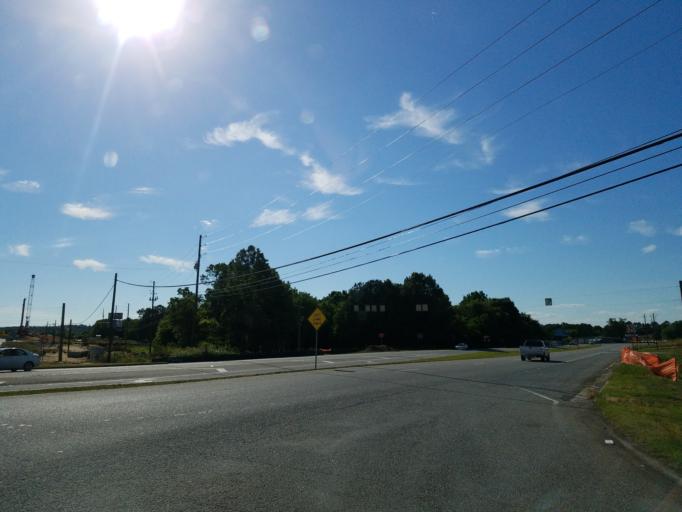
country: US
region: Georgia
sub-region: Bartow County
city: Adairsville
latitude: 34.3770
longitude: -84.9324
